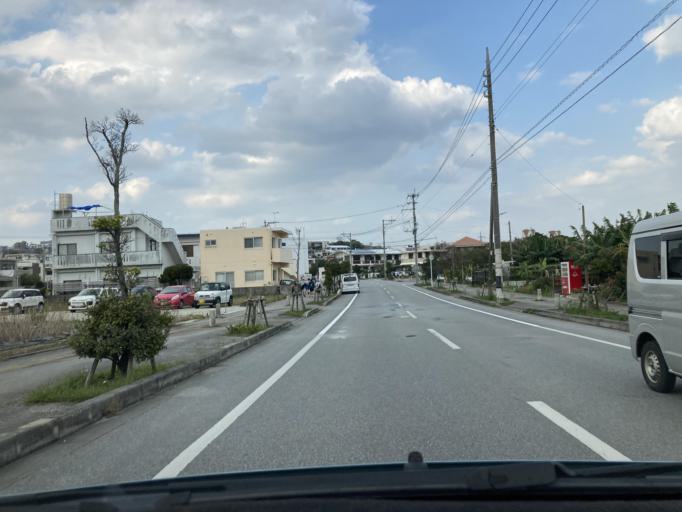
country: JP
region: Okinawa
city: Tomigusuku
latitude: 26.1937
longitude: 127.7333
